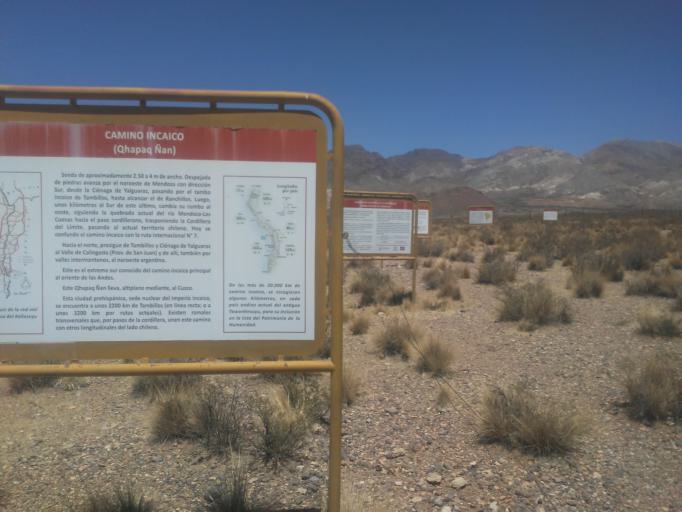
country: AR
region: Mendoza
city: Las Heras
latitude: -32.3844
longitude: -69.3902
